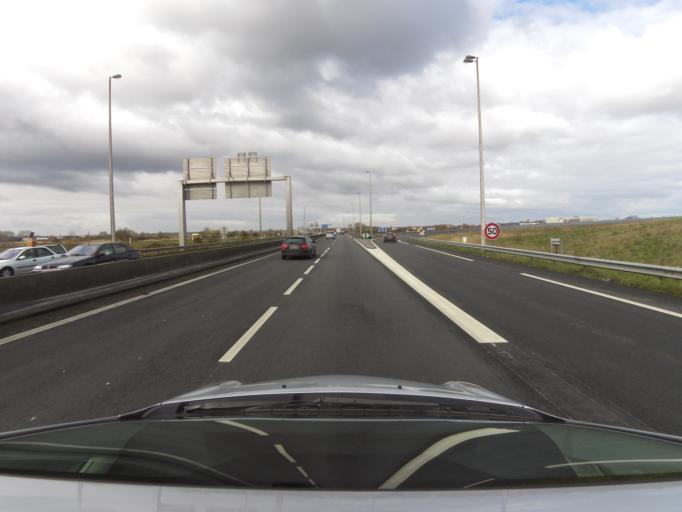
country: FR
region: Nord-Pas-de-Calais
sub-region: Departement du Pas-de-Calais
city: Coulogne
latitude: 50.9360
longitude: 1.9065
